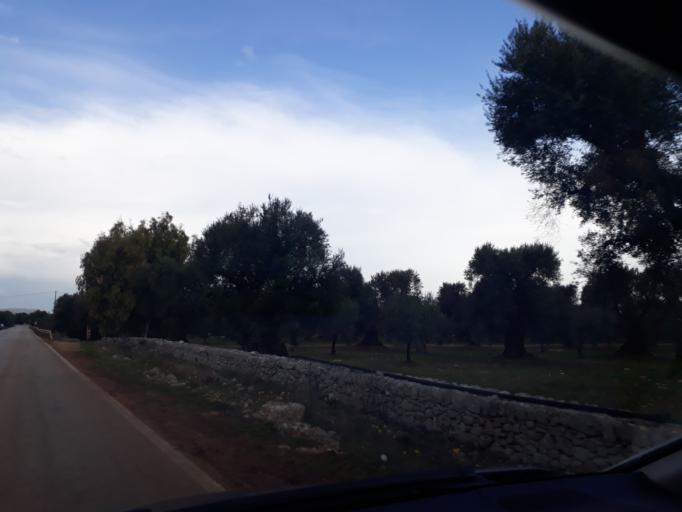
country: IT
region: Apulia
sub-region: Provincia di Brindisi
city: Pezze di Greco
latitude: 40.8099
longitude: 17.3864
